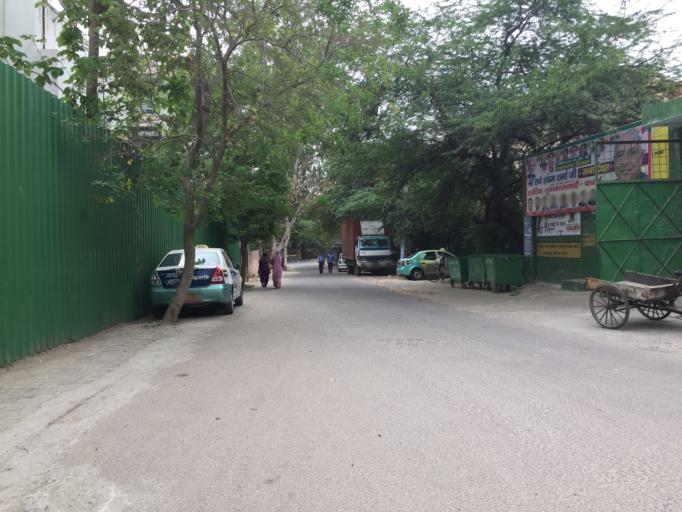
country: IN
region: NCT
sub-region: Central Delhi
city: Karol Bagh
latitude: 28.5602
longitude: 77.1534
